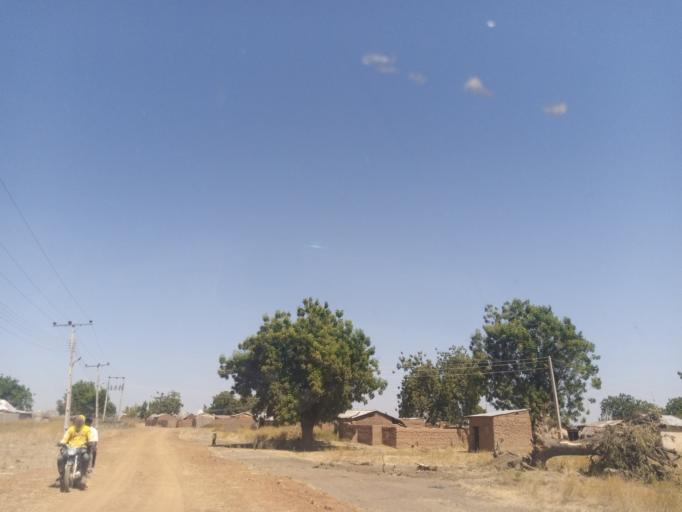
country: NG
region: Adamawa
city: Yola
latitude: 9.3101
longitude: 12.8900
